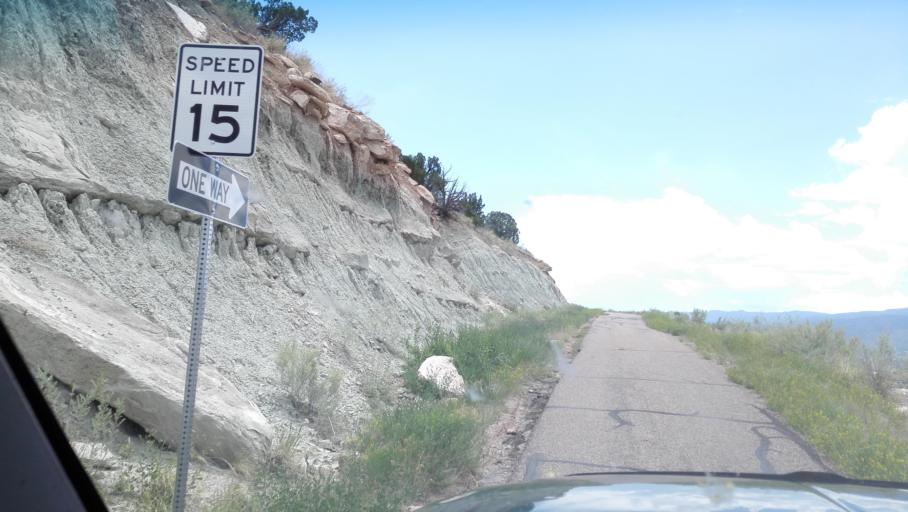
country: US
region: Colorado
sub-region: Fremont County
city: Canon City
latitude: 38.4704
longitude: -105.2556
